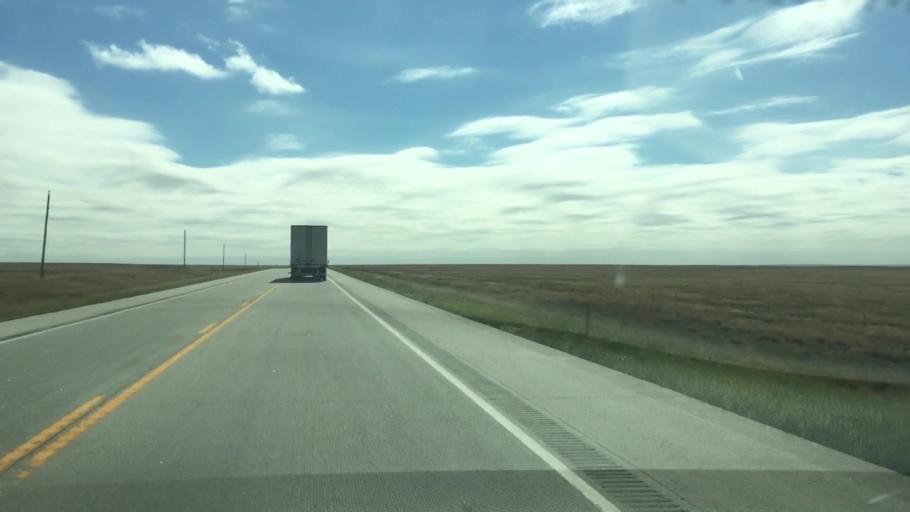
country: US
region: Colorado
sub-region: Lincoln County
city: Hugo
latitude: 39.0197
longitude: -103.3103
